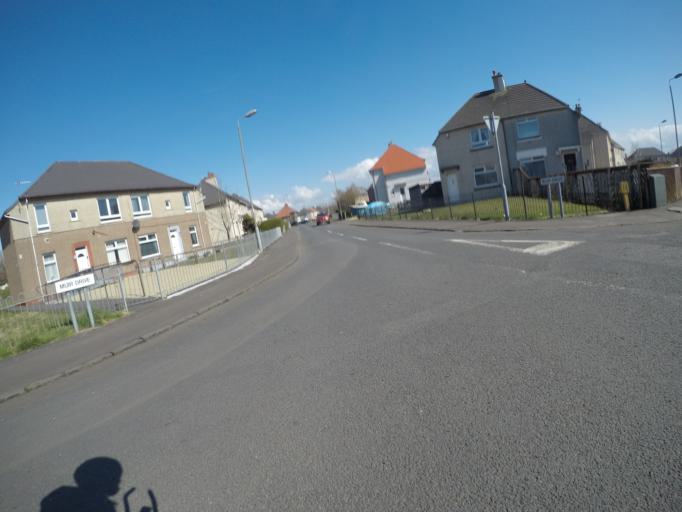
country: GB
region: Scotland
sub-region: North Ayrshire
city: Irvine
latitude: 55.6180
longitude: -4.6549
